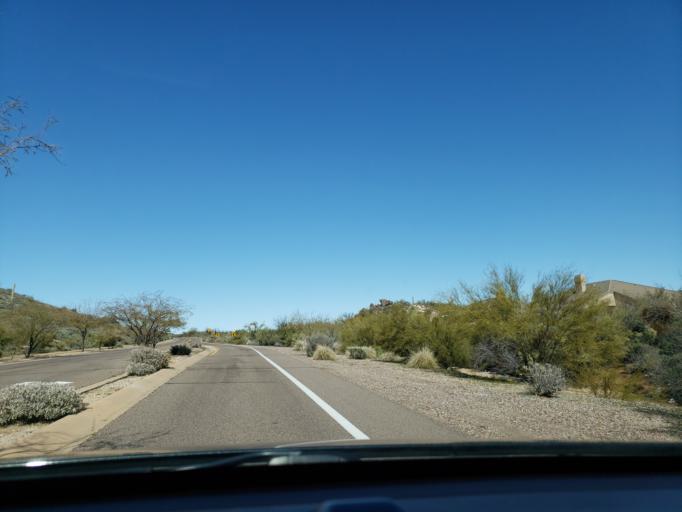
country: US
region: Arizona
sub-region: Maricopa County
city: Carefree
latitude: 33.7108
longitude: -111.8287
